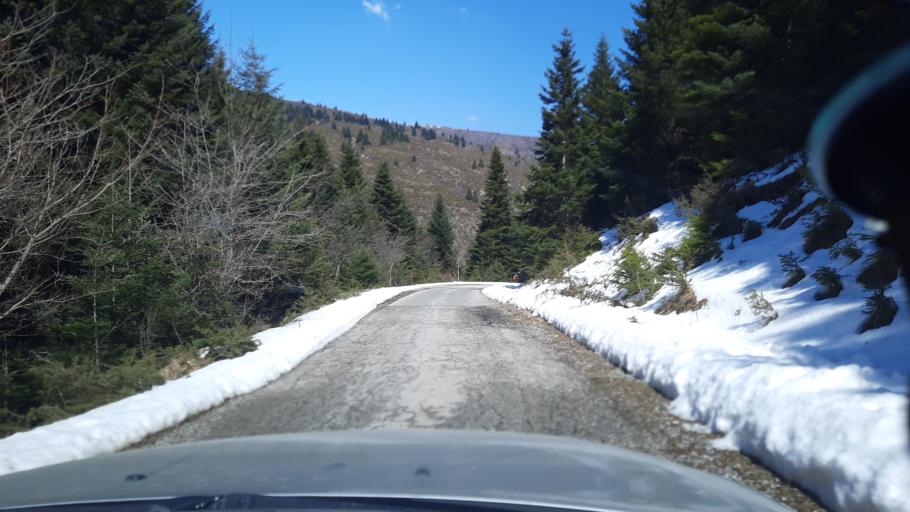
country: MK
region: Gostivar
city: Vrutok
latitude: 41.7177
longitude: 20.7275
